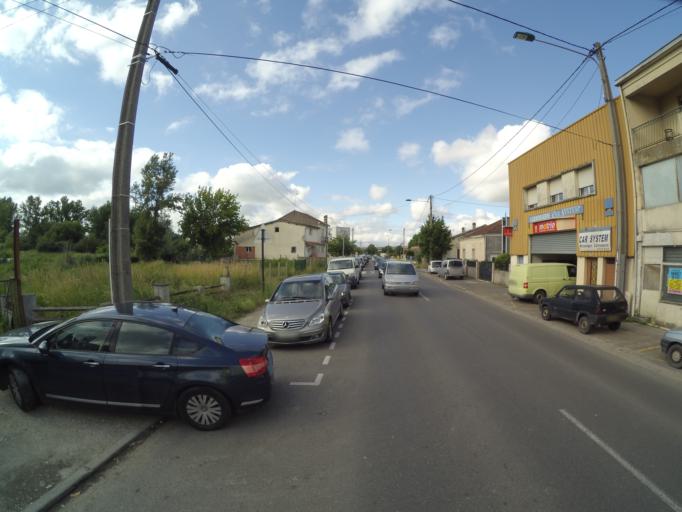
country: FR
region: Aquitaine
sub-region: Departement de la Gironde
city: Lormont
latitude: 44.8788
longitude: -0.5525
